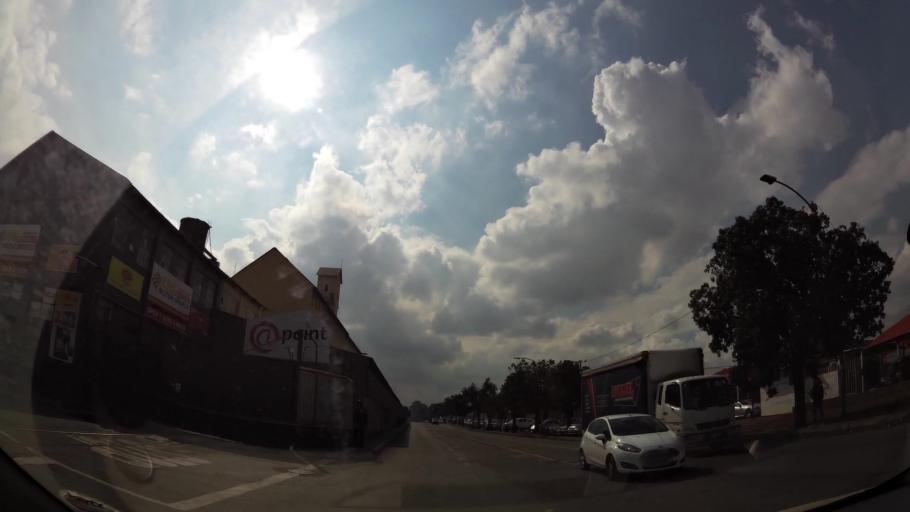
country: ZA
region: Gauteng
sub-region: Sedibeng District Municipality
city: Vereeniging
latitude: -26.6713
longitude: 27.9346
